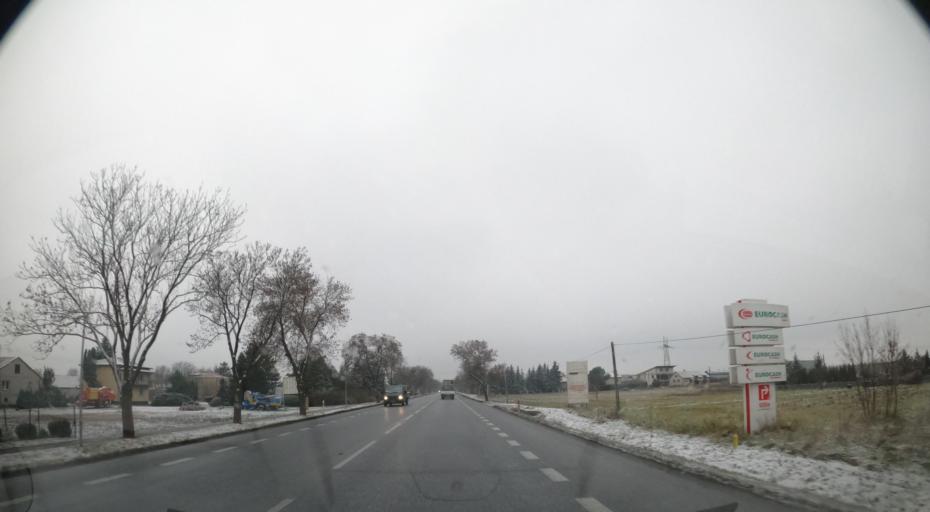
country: PL
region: Masovian Voivodeship
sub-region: Powiat warszawski zachodni
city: Blonie
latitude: 52.1994
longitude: 20.5977
